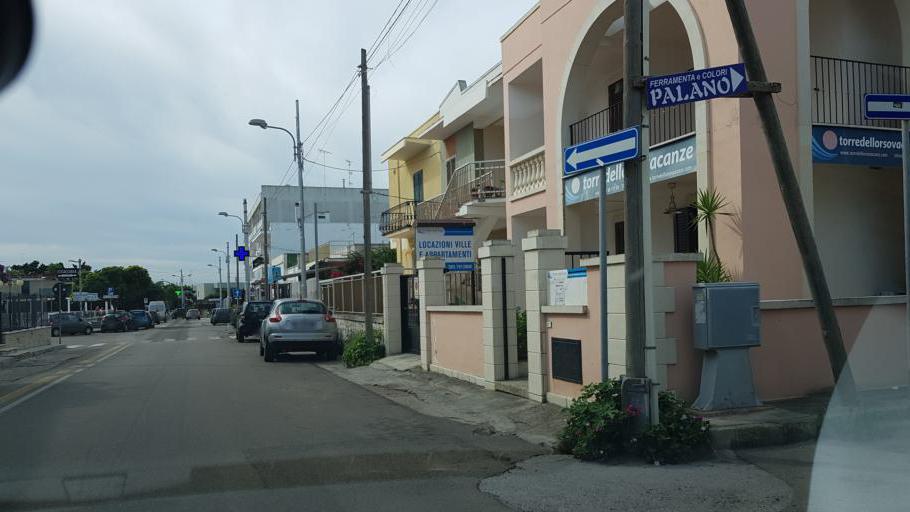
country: IT
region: Apulia
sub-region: Provincia di Lecce
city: Borgagne
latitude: 40.2747
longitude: 18.4284
